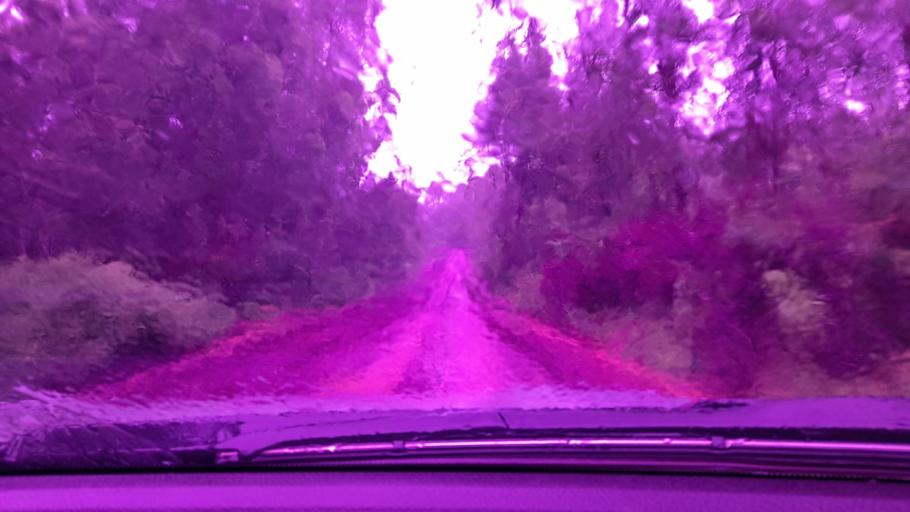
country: ET
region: Oromiya
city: Metu
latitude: 8.3553
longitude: 35.5962
